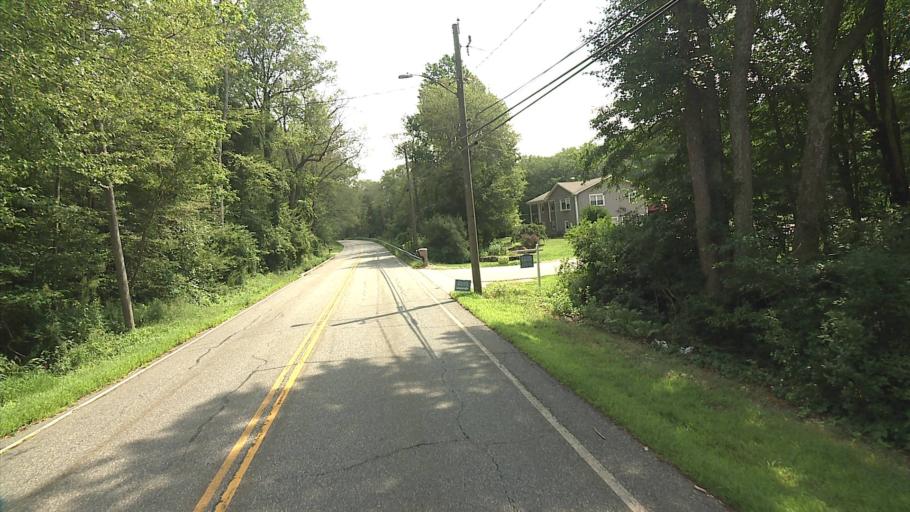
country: US
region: Connecticut
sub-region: New London County
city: Montville Center
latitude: 41.5030
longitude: -72.1971
